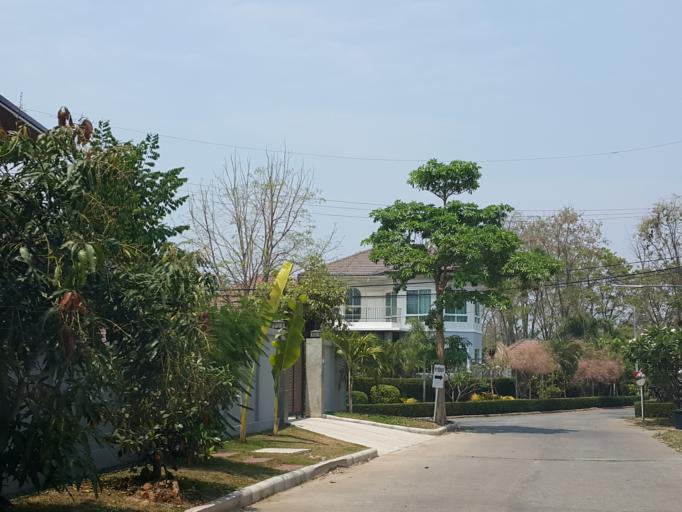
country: TH
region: Chiang Mai
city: Chiang Mai
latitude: 18.7297
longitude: 98.9717
